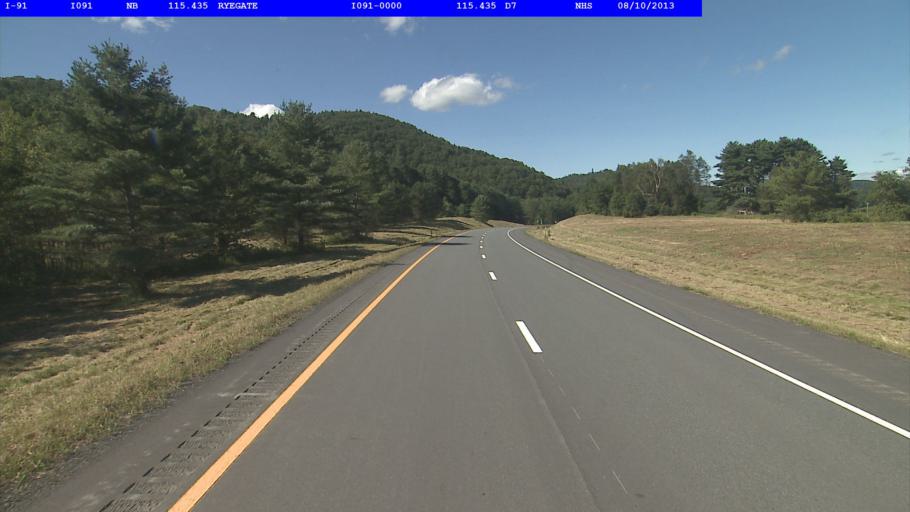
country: US
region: New Hampshire
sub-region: Grafton County
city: Woodsville
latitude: 44.2310
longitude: -72.0688
